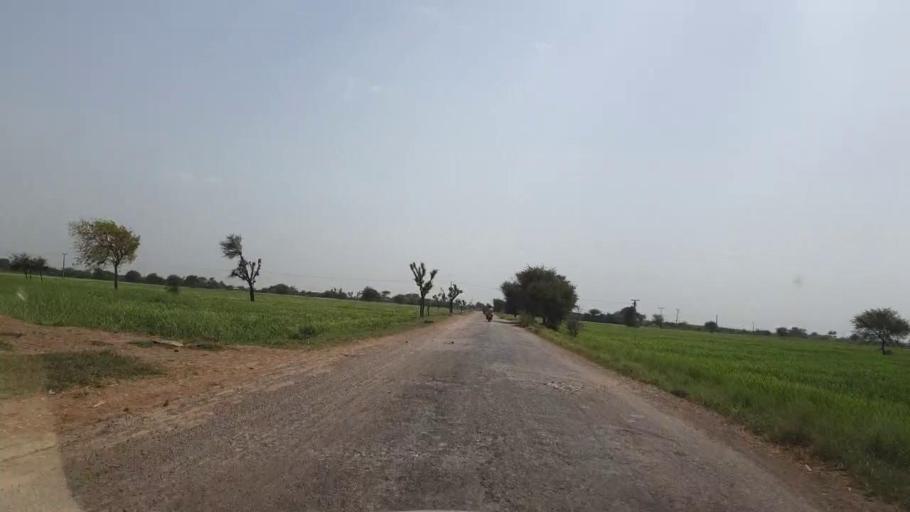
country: PK
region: Sindh
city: Tando Ghulam Ali
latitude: 25.0684
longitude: 68.8230
